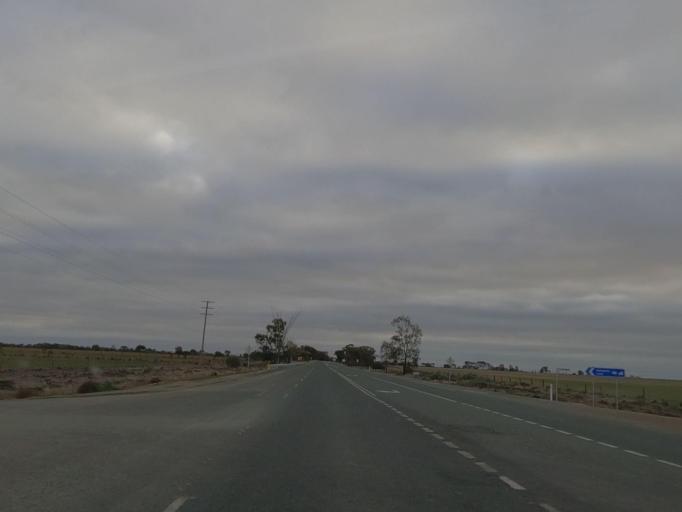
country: AU
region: Victoria
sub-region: Swan Hill
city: Swan Hill
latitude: -35.5513
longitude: 143.7698
